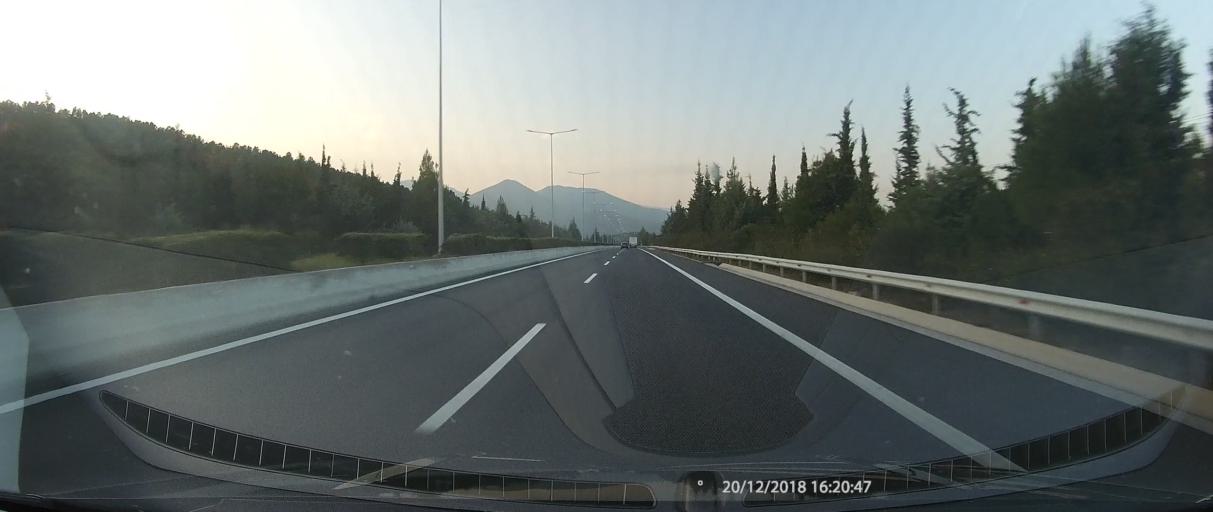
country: GR
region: Thessaly
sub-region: Nomos Magnisias
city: Pteleos
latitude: 39.0356
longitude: 22.9029
